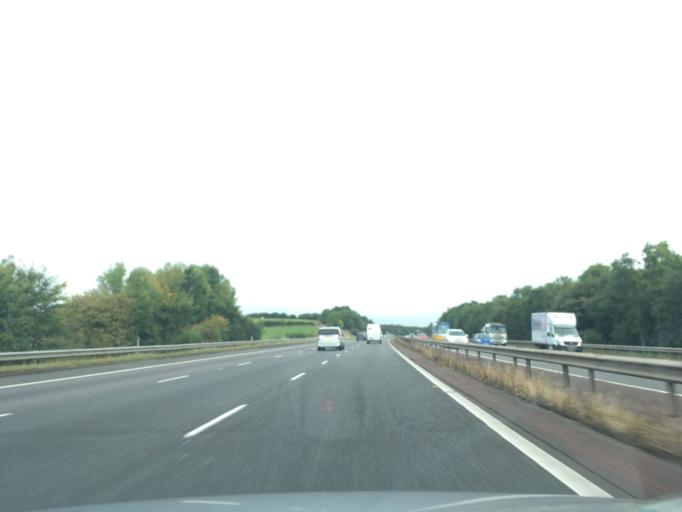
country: GB
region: England
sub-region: Oxfordshire
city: Adderbury
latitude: 52.0259
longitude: -1.2966
